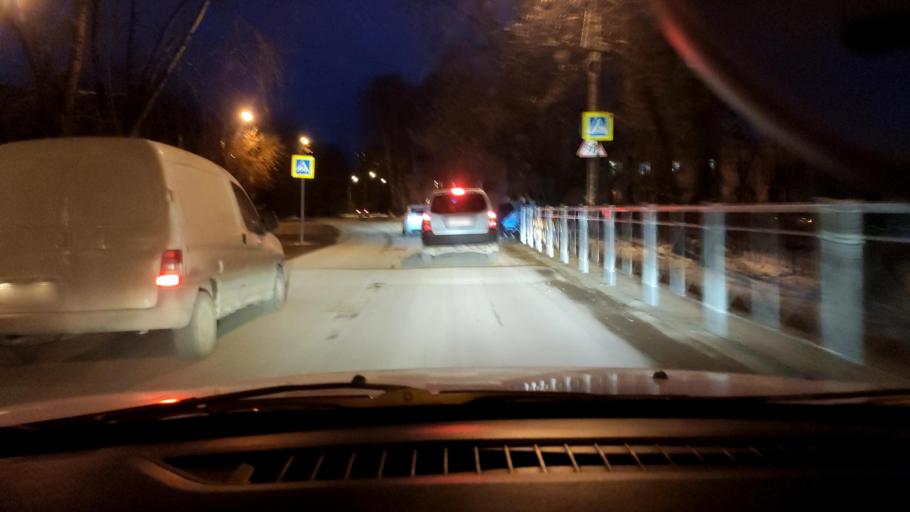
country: RU
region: Perm
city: Kultayevo
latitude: 58.0063
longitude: 55.9597
